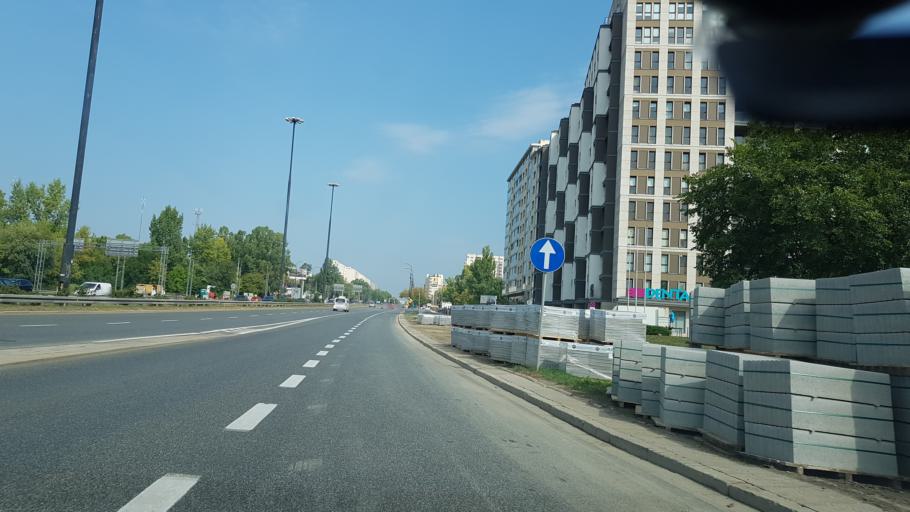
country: PL
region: Masovian Voivodeship
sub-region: Warszawa
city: Mokotow
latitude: 52.1685
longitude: 21.0185
